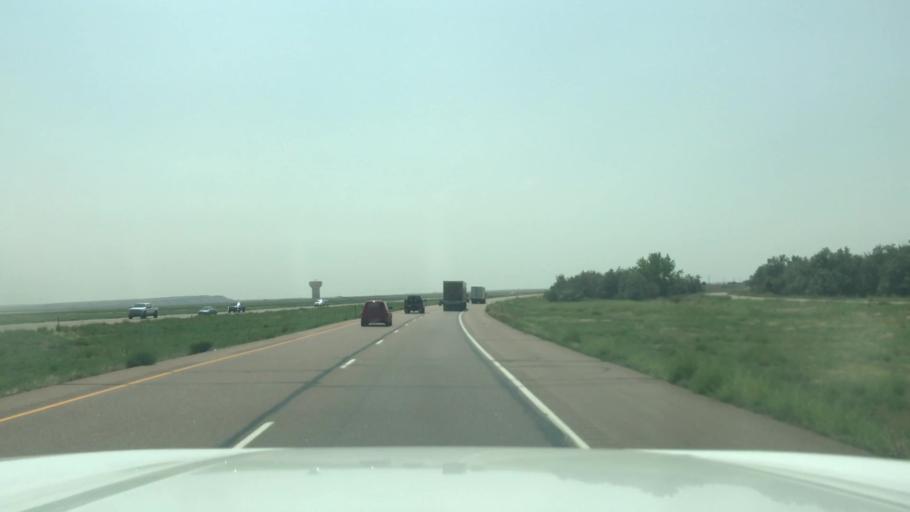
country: US
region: Colorado
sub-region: Pueblo County
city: Pueblo
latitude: 38.1758
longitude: -104.6347
